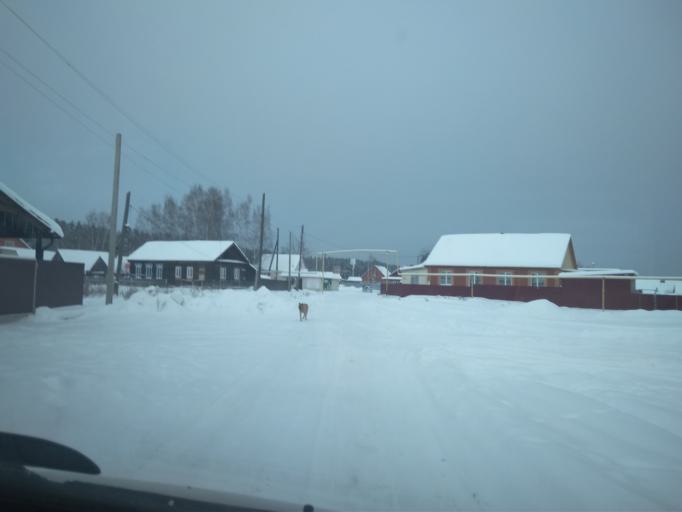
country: RU
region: Mordoviya
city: Kemlya
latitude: 54.7236
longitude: 45.2841
